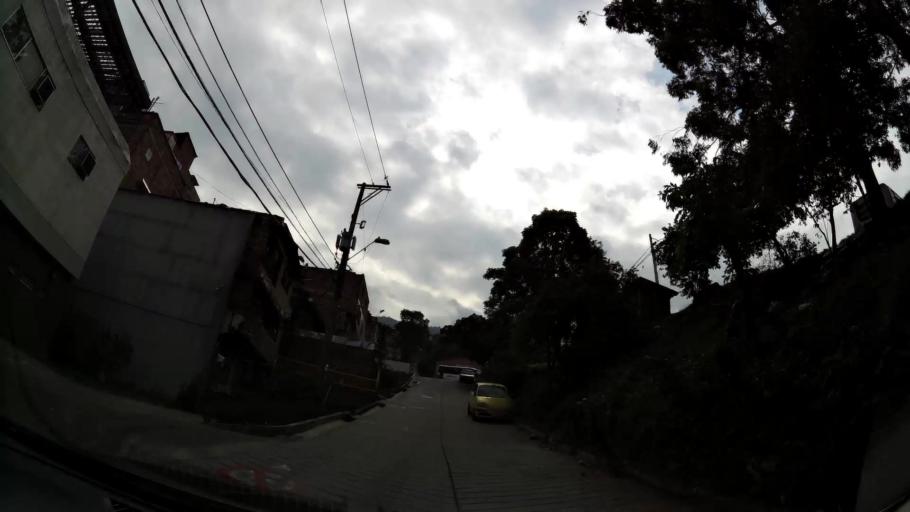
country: CO
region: Antioquia
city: Medellin
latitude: 6.2877
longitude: -75.5524
